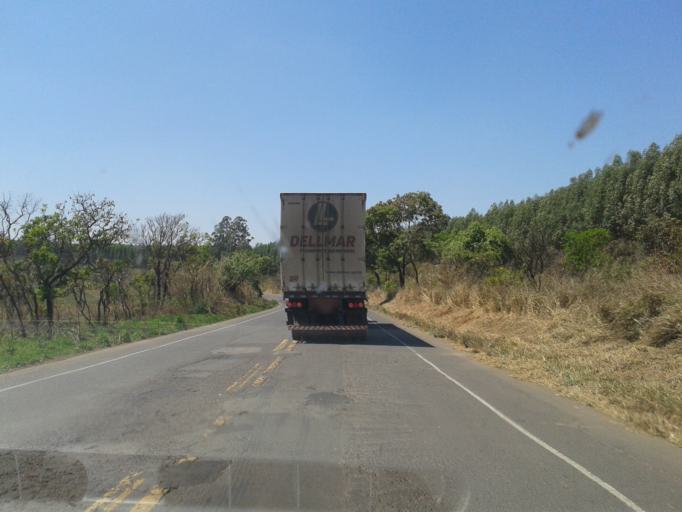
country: BR
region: Minas Gerais
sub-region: Araxa
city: Araxa
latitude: -19.4358
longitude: -47.2136
